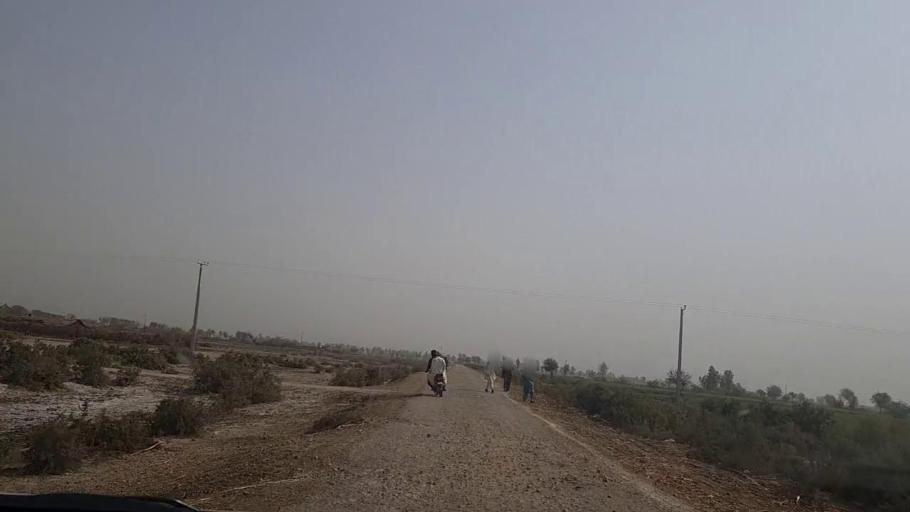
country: PK
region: Sindh
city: Pithoro
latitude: 25.4740
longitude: 69.2266
